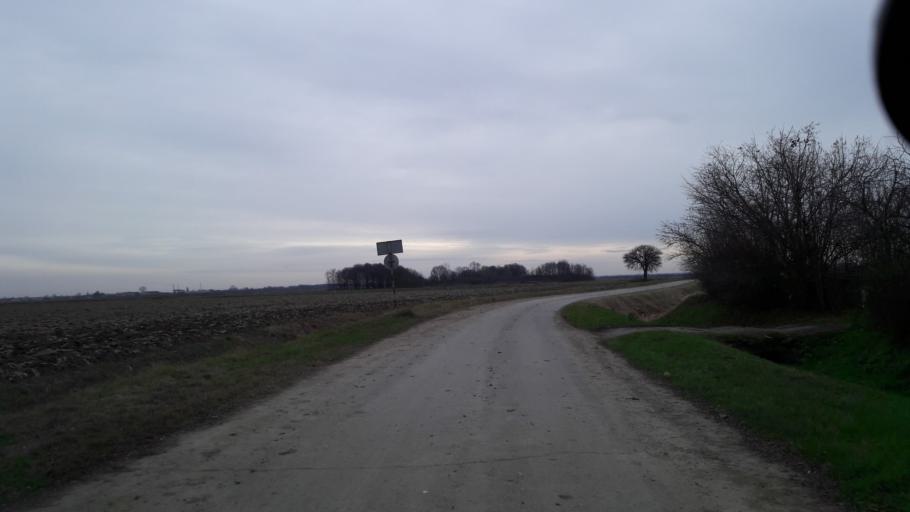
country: HR
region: Osjecko-Baranjska
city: Vladislavci
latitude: 45.4448
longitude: 18.5631
